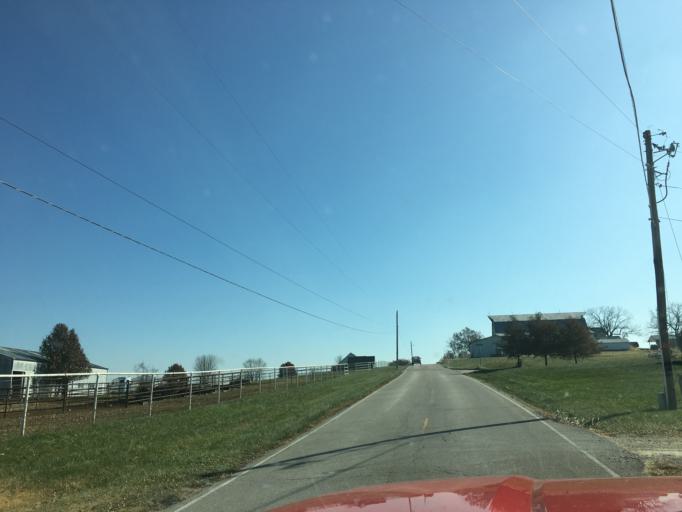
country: US
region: Missouri
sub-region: Cole County
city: Wardsville
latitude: 38.5002
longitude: -92.1840
